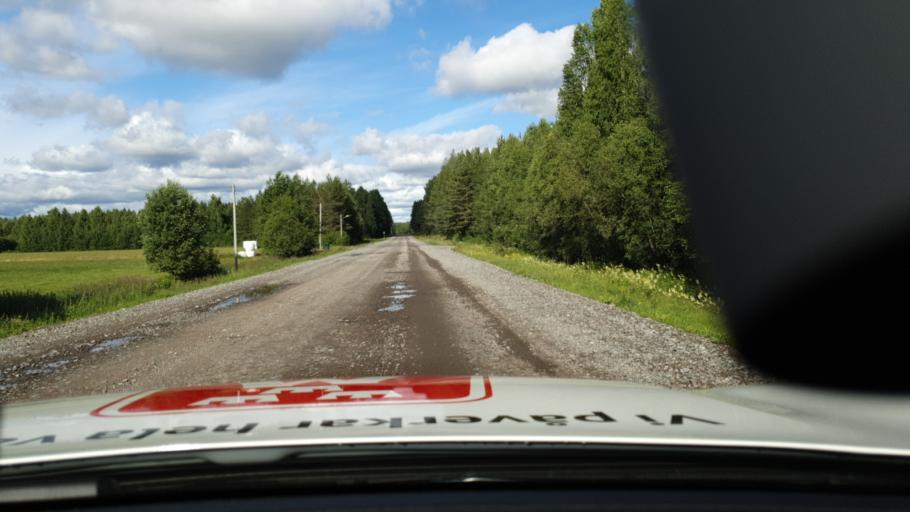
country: SE
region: Norrbotten
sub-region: Bodens Kommun
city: Boden
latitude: 65.8593
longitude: 21.4559
